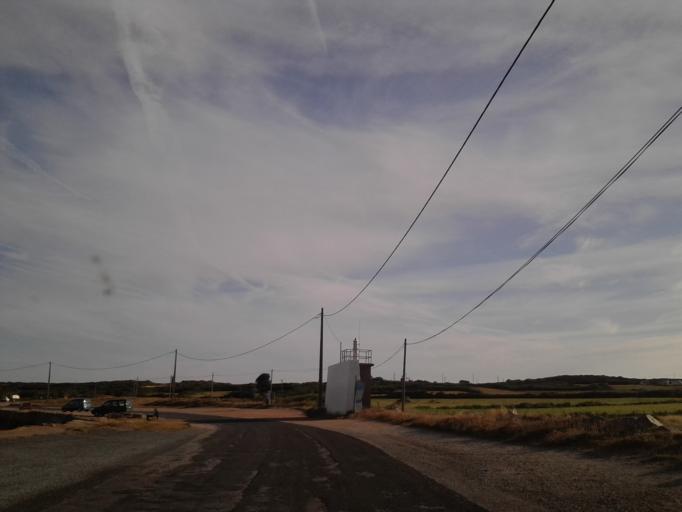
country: FR
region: Lower Normandy
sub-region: Departement de la Manche
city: Fermanville
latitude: 49.6867
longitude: -1.4724
